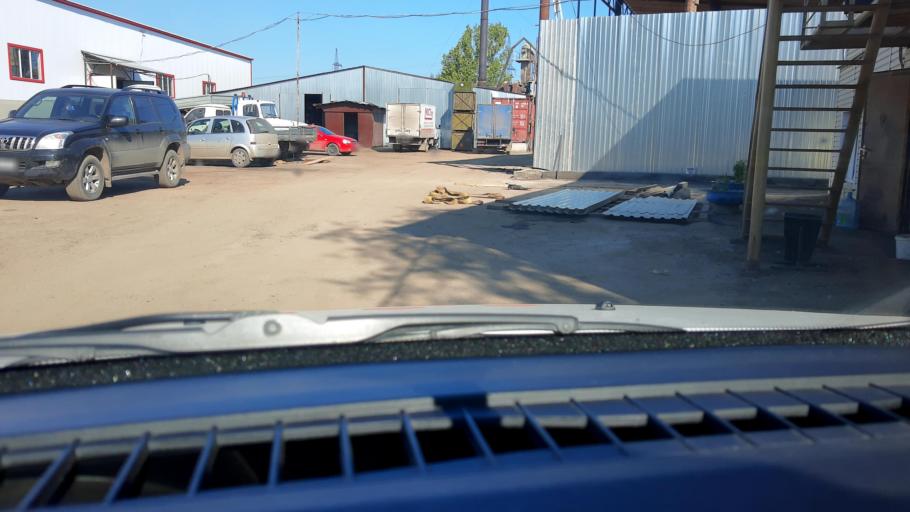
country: RU
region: Nizjnij Novgorod
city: Gorbatovka
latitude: 56.2752
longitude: 43.8518
